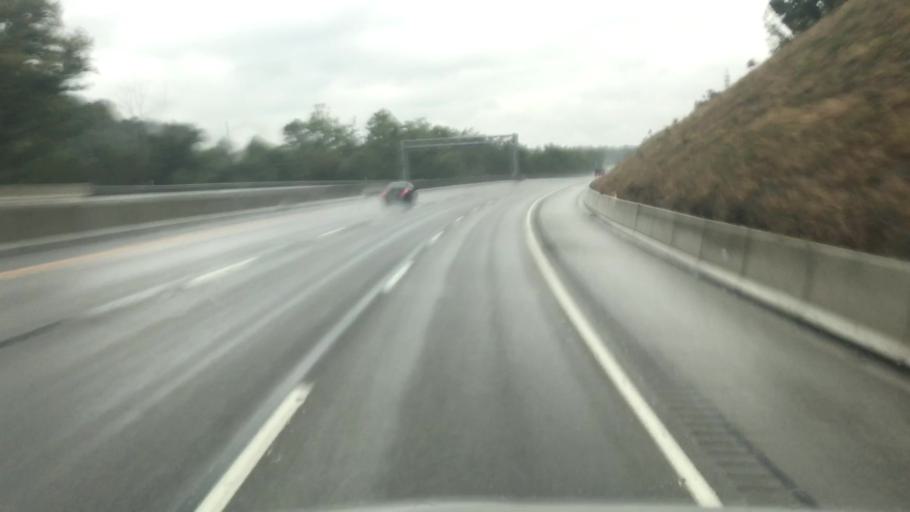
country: US
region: Pennsylvania
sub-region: Allegheny County
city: Oakmont
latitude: 40.5567
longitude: -79.8476
